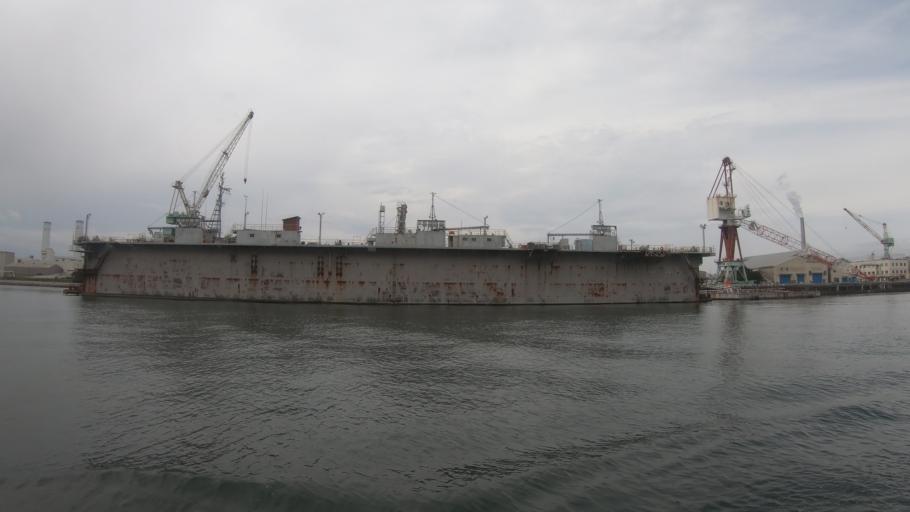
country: JP
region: Kanagawa
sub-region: Kawasaki-shi
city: Kawasaki
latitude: 35.4890
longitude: 139.6921
